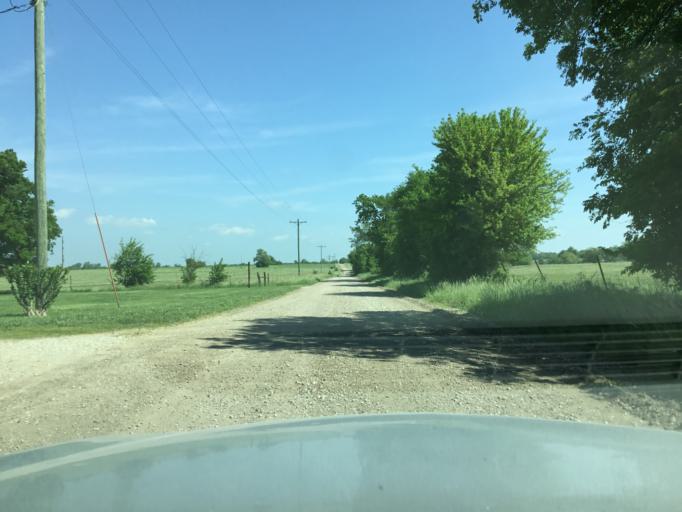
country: US
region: Kansas
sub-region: Labette County
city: Oswego
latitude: 37.1747
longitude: -95.1399
